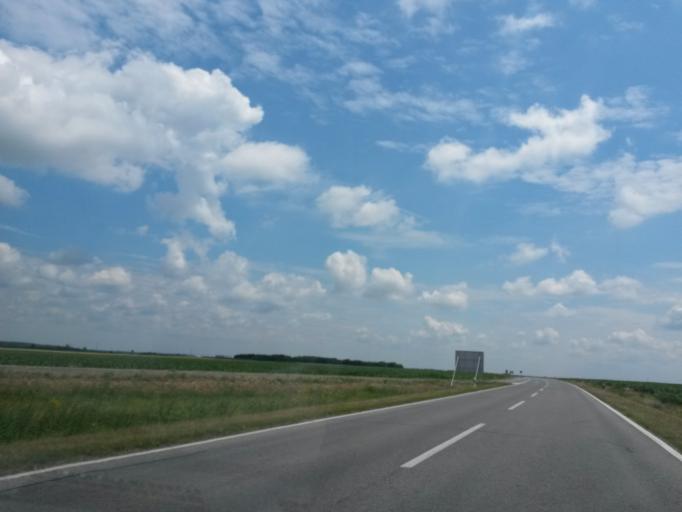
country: HR
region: Osjecko-Baranjska
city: Tenja
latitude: 45.5300
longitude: 18.7447
